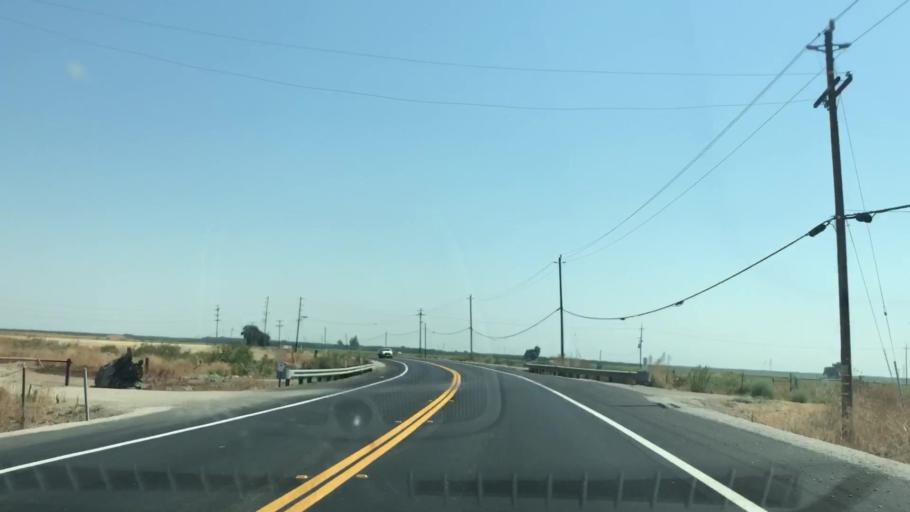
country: US
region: California
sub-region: San Joaquin County
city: Garden Acres
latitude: 37.9494
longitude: -121.1828
